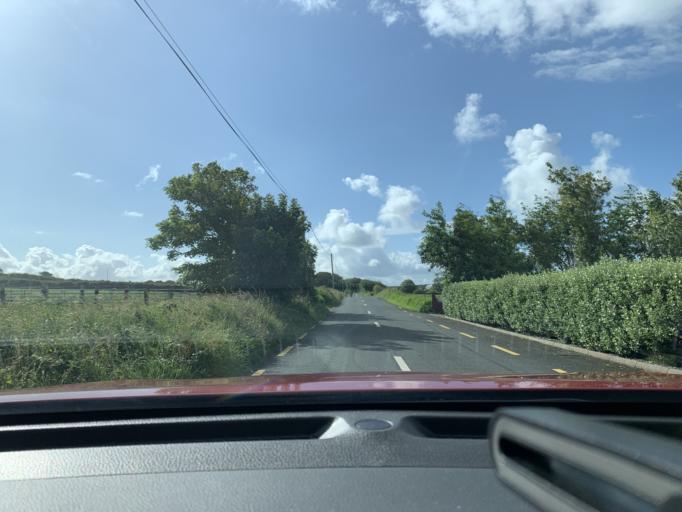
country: IE
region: Connaught
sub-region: Sligo
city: Strandhill
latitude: 54.3597
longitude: -8.6125
